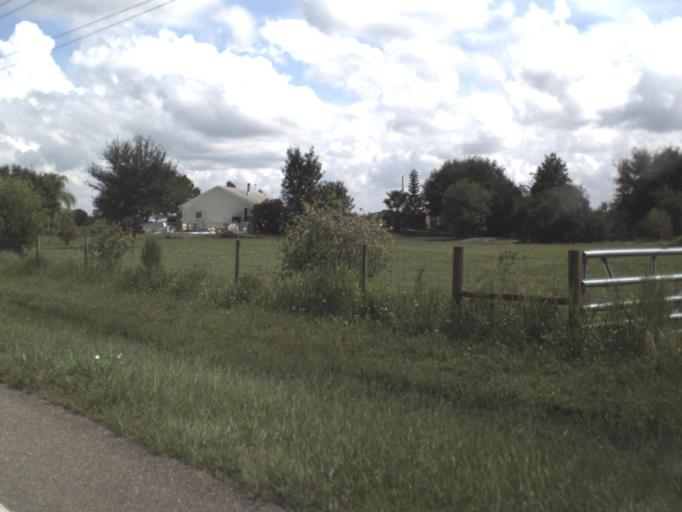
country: US
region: Florida
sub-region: Hardee County
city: Wauchula
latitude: 27.4852
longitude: -82.0070
